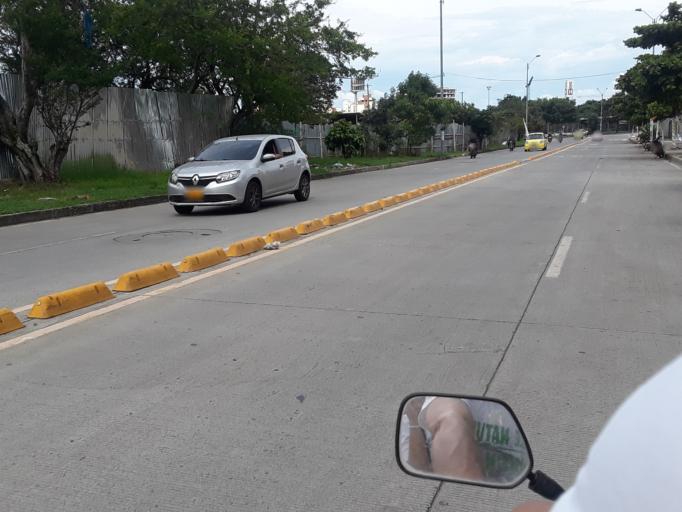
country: CO
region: Valle del Cauca
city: Cali
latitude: 3.4164
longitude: -76.5510
